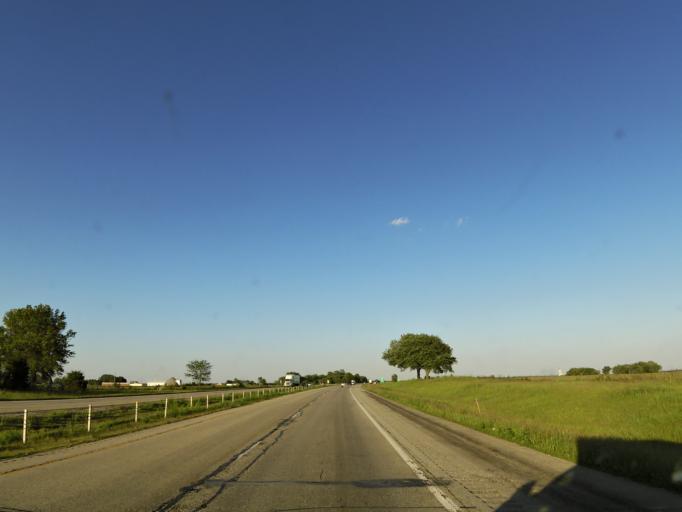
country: US
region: Illinois
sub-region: Champaign County
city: Homer
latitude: 40.1231
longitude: -87.9197
